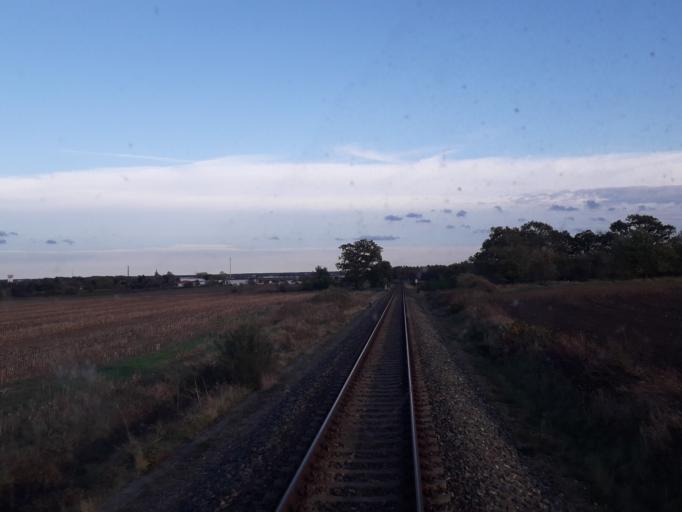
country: DE
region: Brandenburg
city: Wittstock
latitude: 53.1584
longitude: 12.4372
